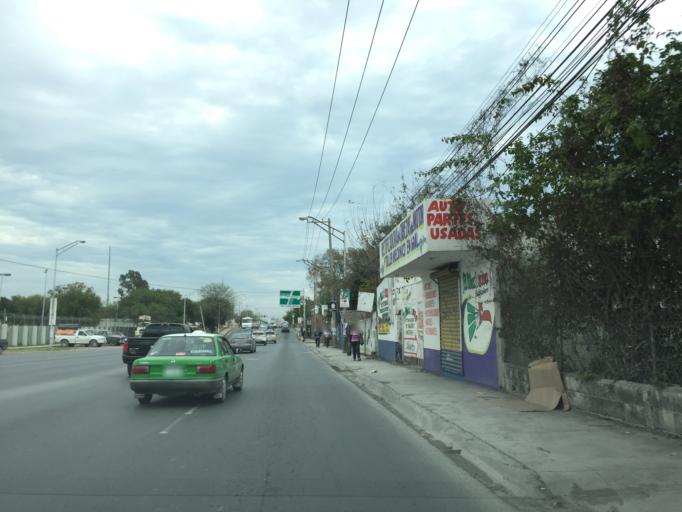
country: MX
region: Nuevo Leon
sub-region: Juarez
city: Valle de Juarez
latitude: 25.6647
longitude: -100.1754
